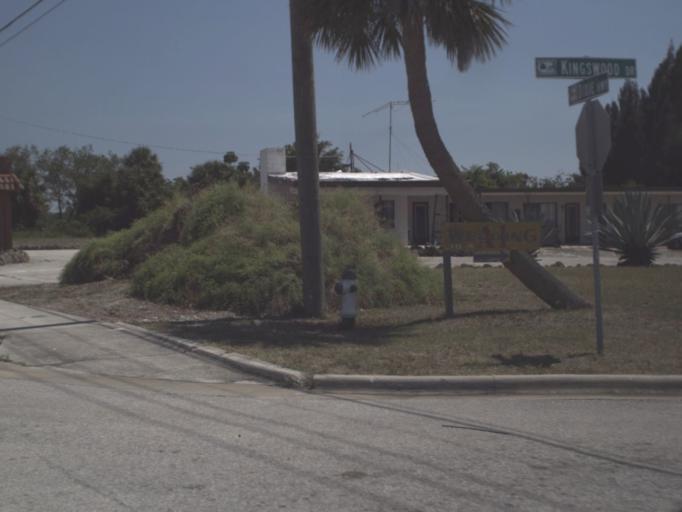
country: US
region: Florida
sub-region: Brevard County
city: Palm Bay
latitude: 28.0568
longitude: -80.5900
